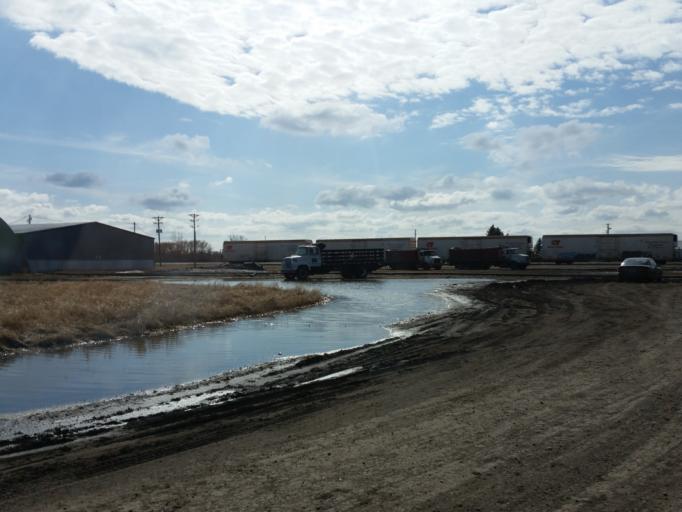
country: US
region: North Dakota
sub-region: Walsh County
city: Grafton
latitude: 48.4320
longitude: -97.4119
